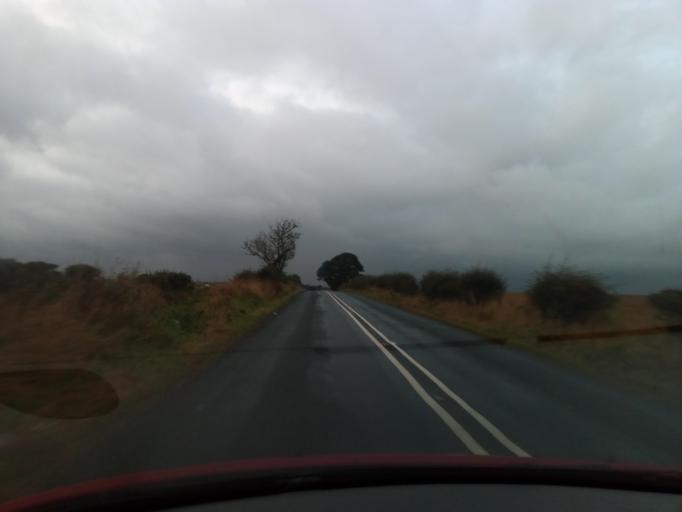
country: GB
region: England
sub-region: Darlington
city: Summerhouse
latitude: 54.6003
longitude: -1.6806
